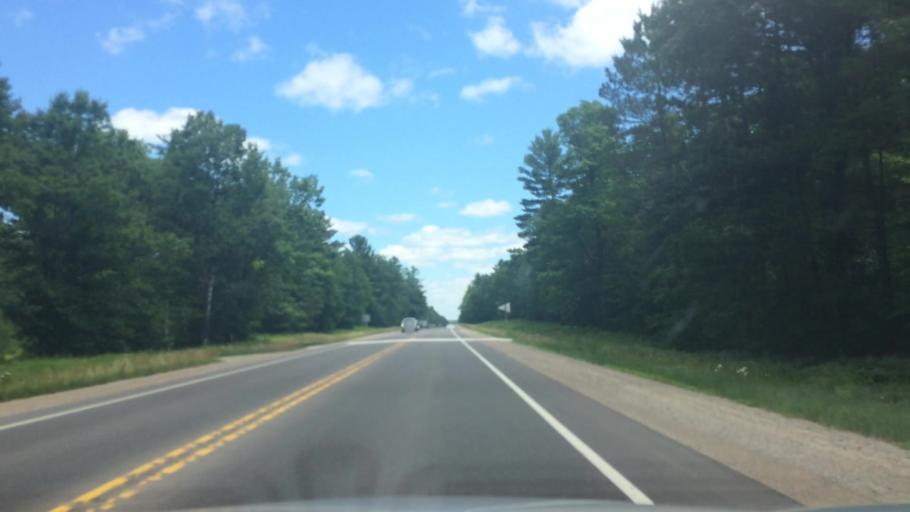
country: US
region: Wisconsin
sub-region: Vilas County
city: Lac du Flambeau
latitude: 45.9839
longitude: -89.6963
